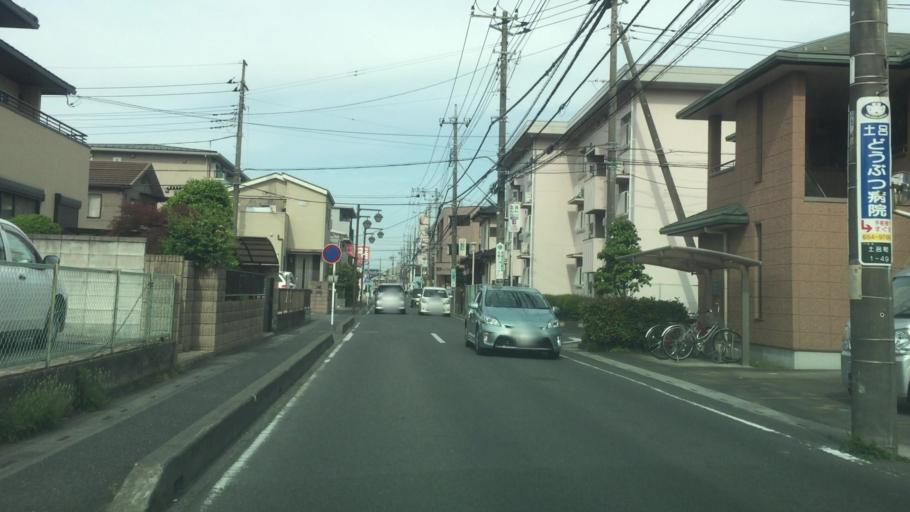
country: JP
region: Saitama
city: Ageoshimo
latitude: 35.9363
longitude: 139.6292
